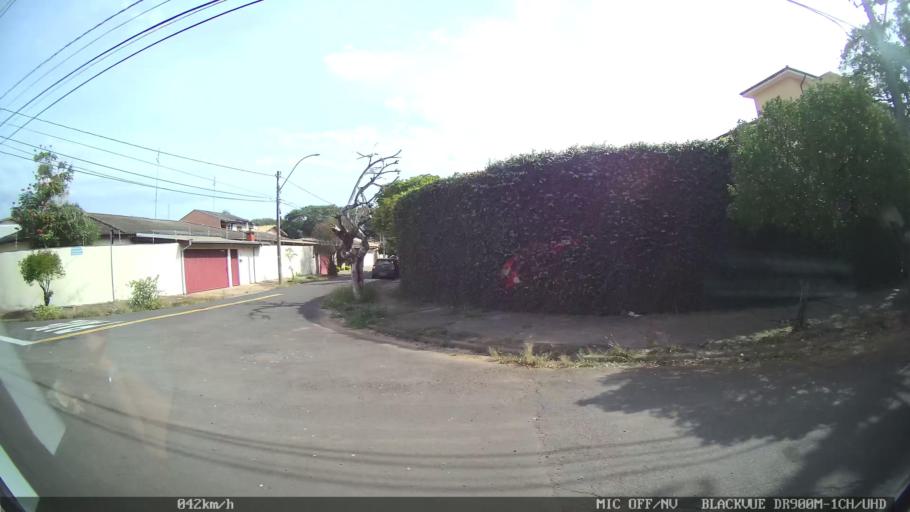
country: BR
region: Sao Paulo
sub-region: Piracicaba
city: Piracicaba
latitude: -22.7098
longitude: -47.6728
